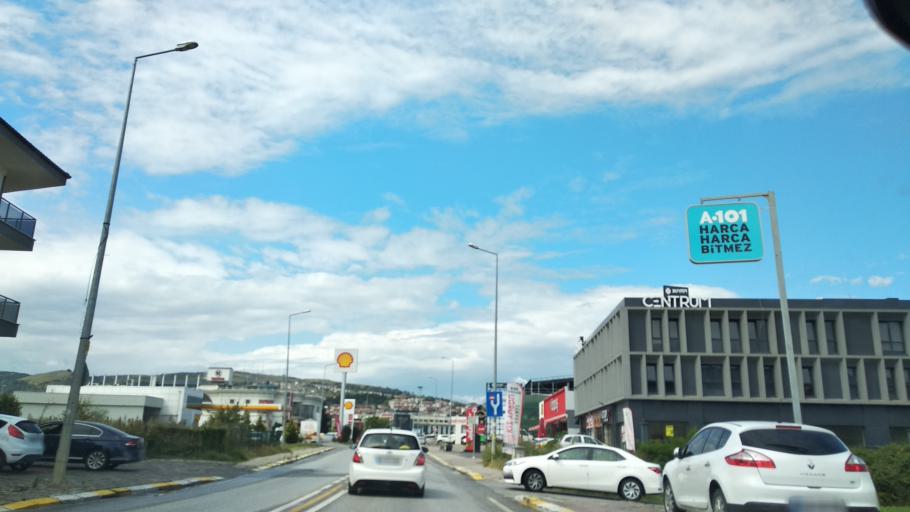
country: TR
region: Sakarya
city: Adapazari
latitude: 40.7586
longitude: 30.3669
